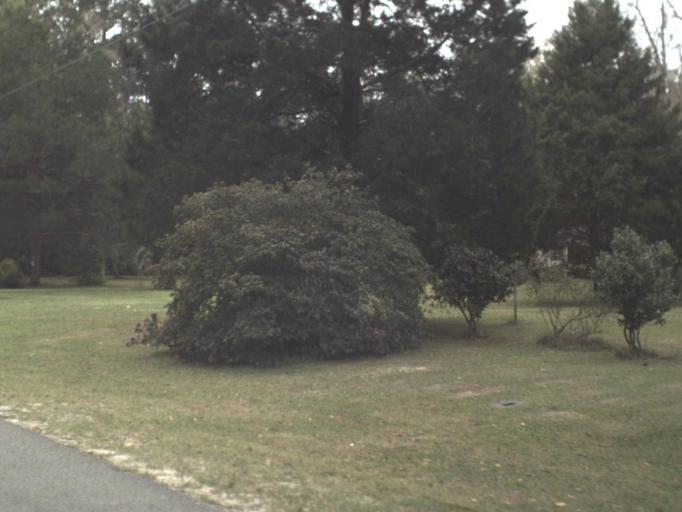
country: US
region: Florida
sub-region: Gulf County
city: Wewahitchka
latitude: 30.0771
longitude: -85.1945
